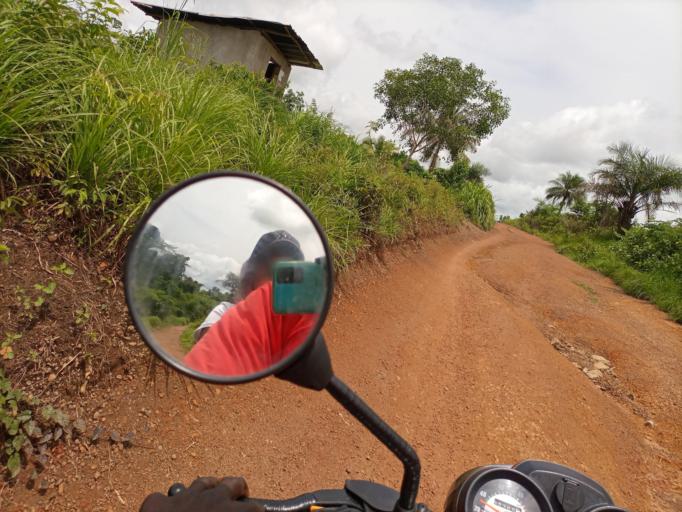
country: SL
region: Southern Province
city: Baoma
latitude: 7.9768
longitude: -11.7127
